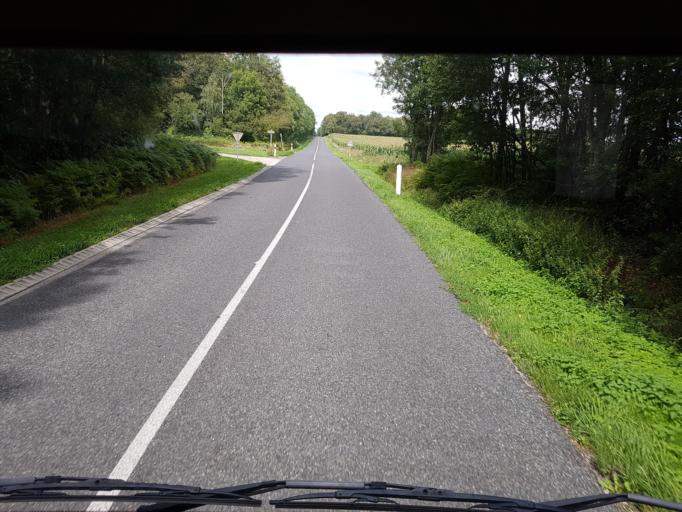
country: FR
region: Rhone-Alpes
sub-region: Departement de l'Ain
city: Perouges
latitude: 45.9256
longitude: 5.1324
